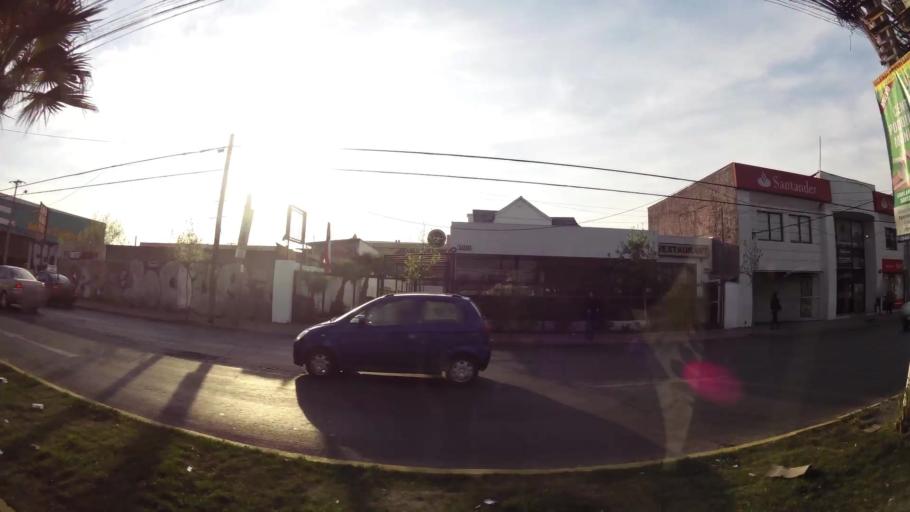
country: CL
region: Santiago Metropolitan
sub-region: Provincia de Santiago
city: La Pintana
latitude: -33.5225
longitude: -70.6603
